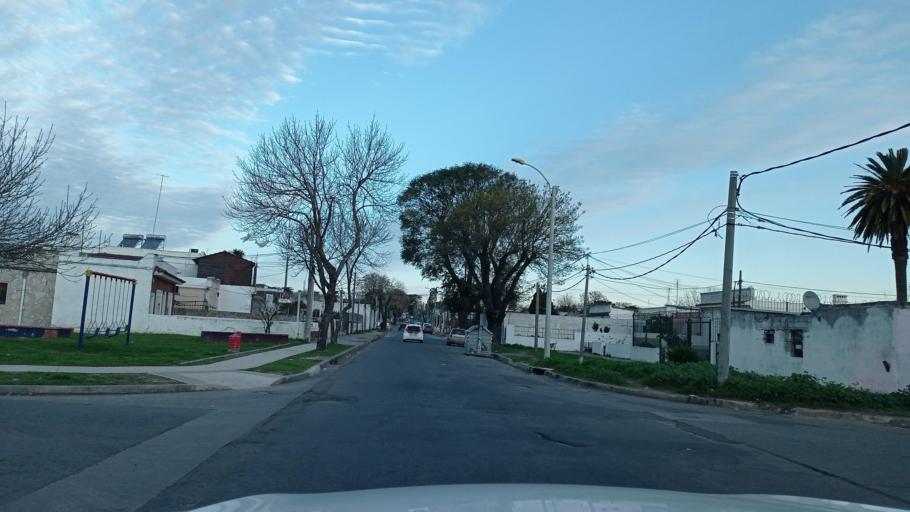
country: UY
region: Montevideo
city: Montevideo
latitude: -34.8680
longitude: -56.1466
